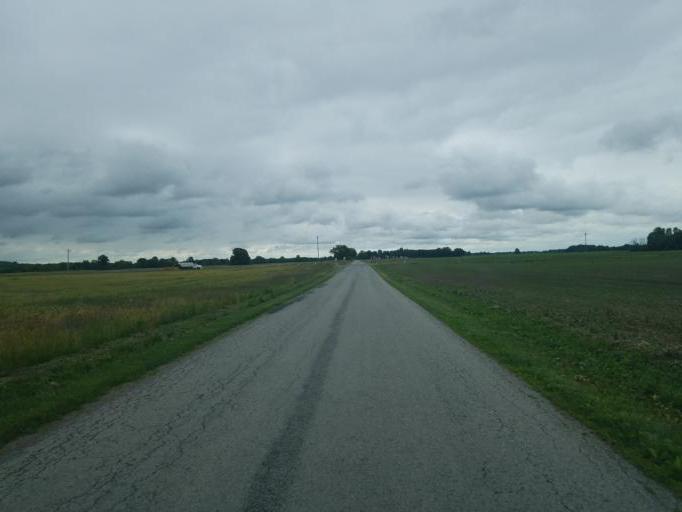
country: US
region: Ohio
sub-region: Morrow County
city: Cardington
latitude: 40.5591
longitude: -82.9194
